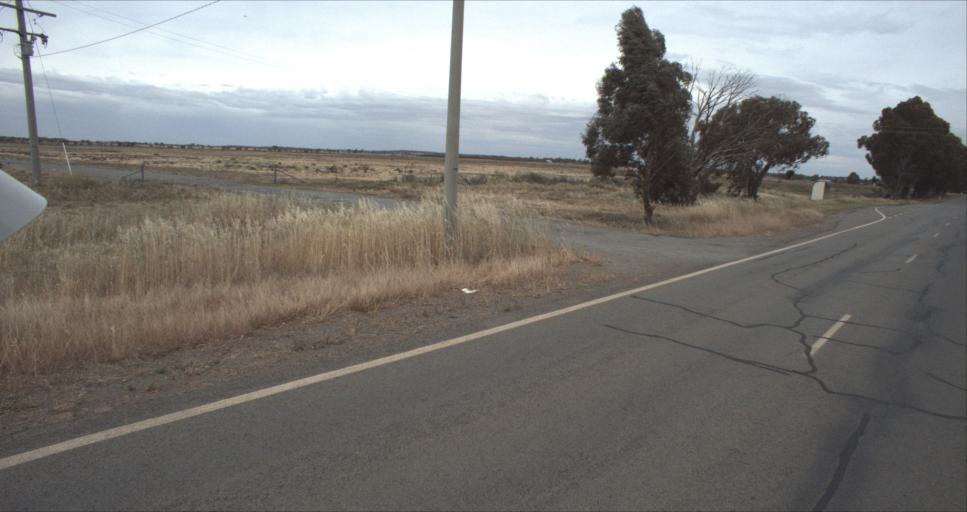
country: AU
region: New South Wales
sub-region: Leeton
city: Leeton
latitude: -34.5186
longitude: 146.4156
